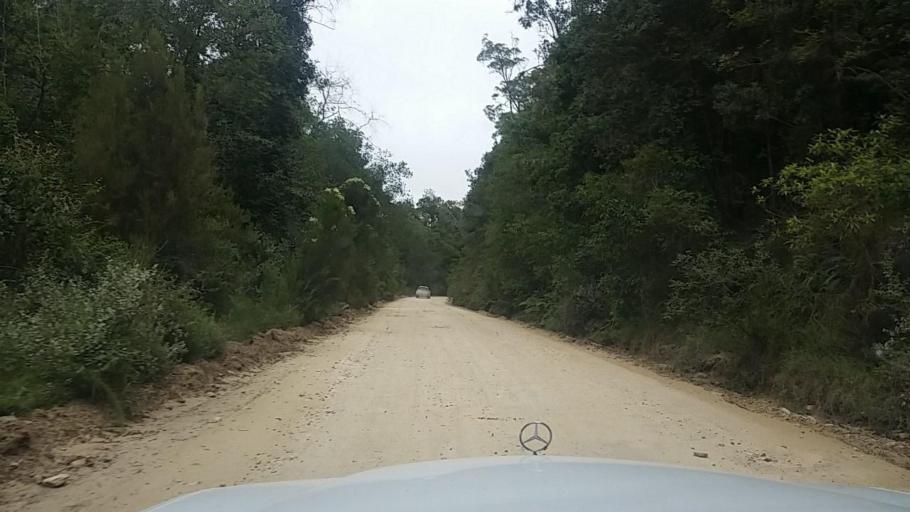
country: ZA
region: Western Cape
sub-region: Eden District Municipality
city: Knysna
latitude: -33.9680
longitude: 23.1491
